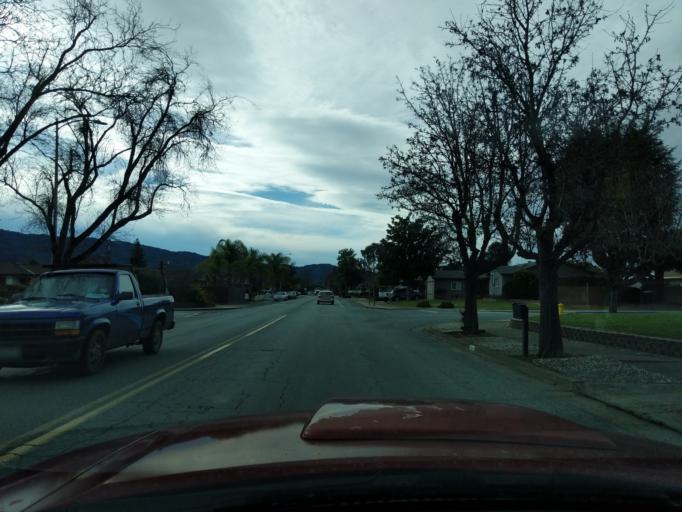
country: US
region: California
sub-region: Santa Clara County
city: Gilroy
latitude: 37.0180
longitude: -121.5814
